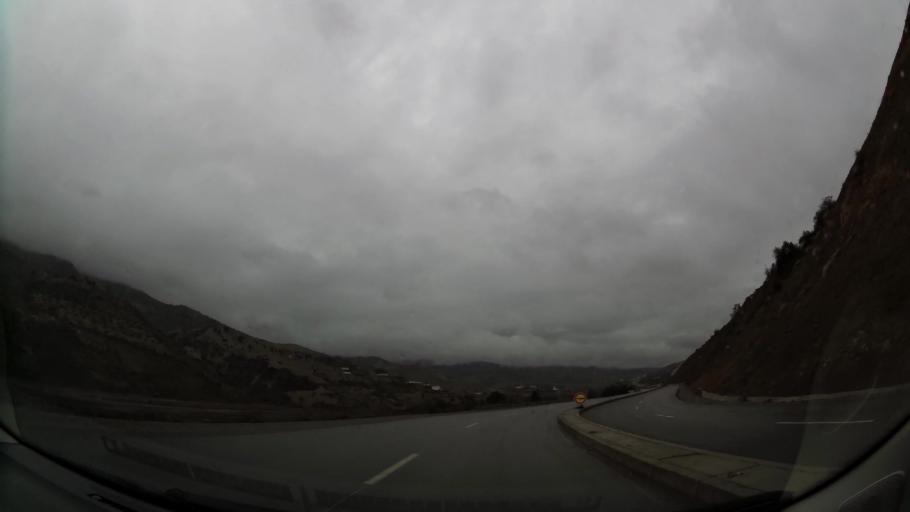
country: MA
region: Taza-Al Hoceima-Taounate
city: Imzourene
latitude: 35.0076
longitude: -3.8121
